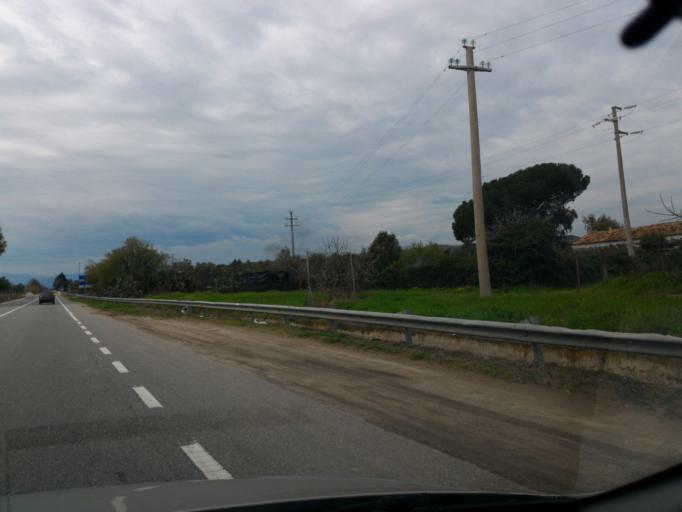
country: IT
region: Calabria
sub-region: Provincia di Catanzaro
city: Barone
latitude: 38.8611
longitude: 16.6785
